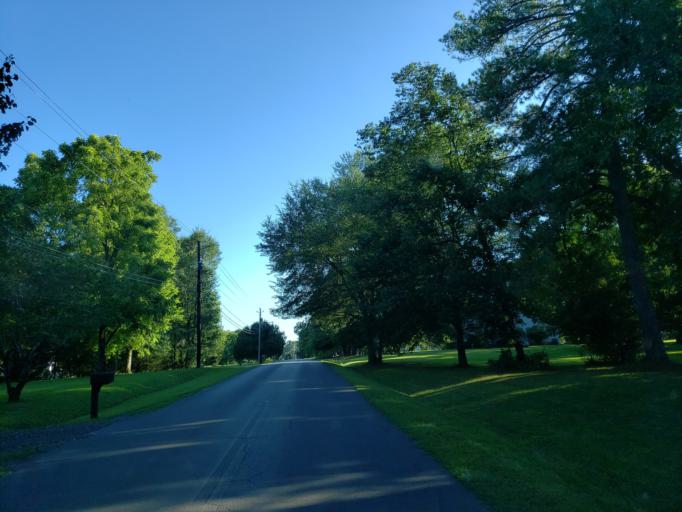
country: US
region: Georgia
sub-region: Polk County
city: Aragon
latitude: 34.0532
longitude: -85.0488
